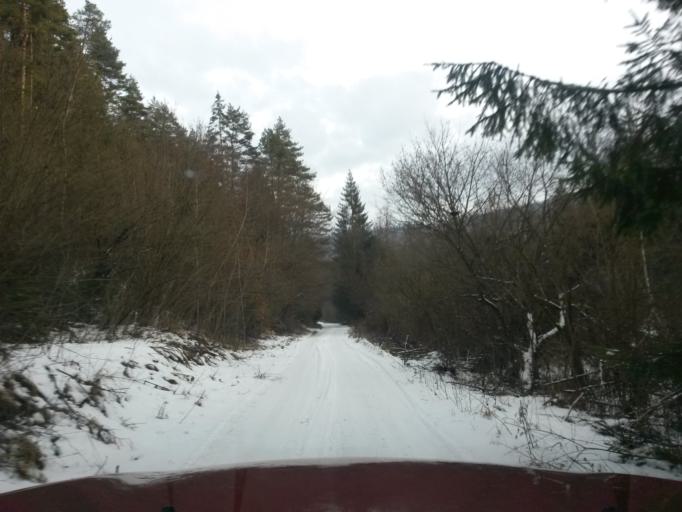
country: SK
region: Kosicky
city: Spisska Nova Ves
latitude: 48.8947
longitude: 20.6266
